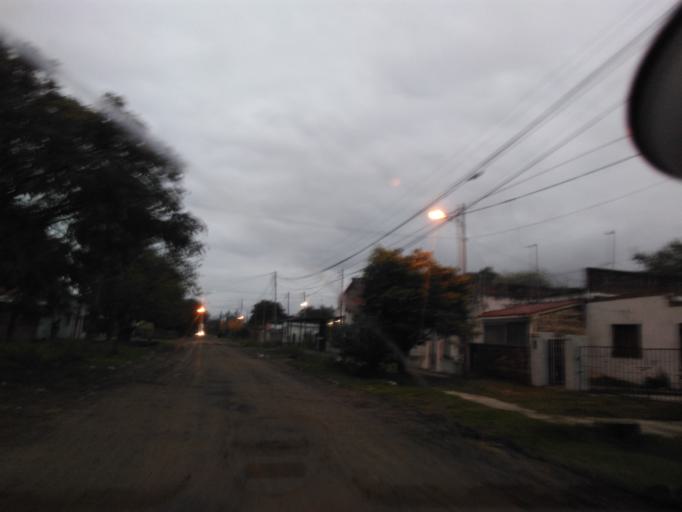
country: AR
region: Chaco
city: Resistencia
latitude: -27.4760
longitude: -58.9895
